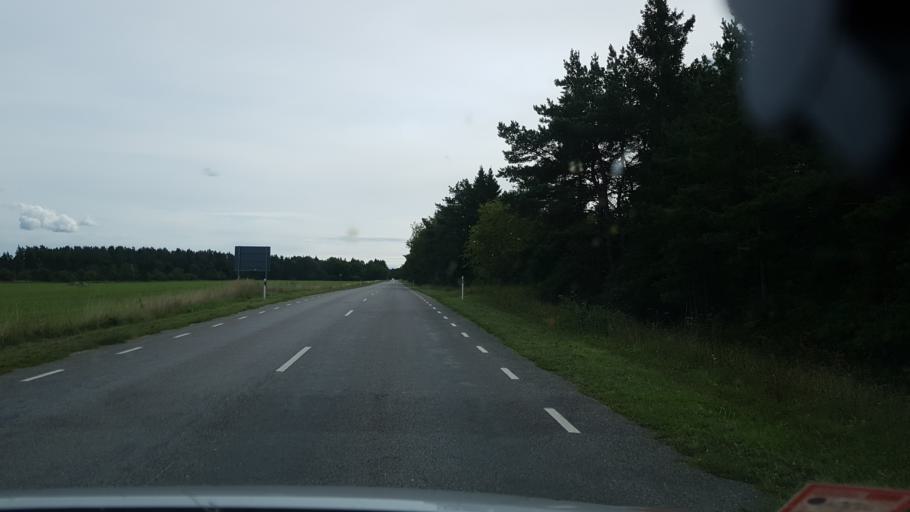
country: EE
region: Saare
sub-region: Kuressaare linn
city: Kuressaare
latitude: 58.3623
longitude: 22.0589
